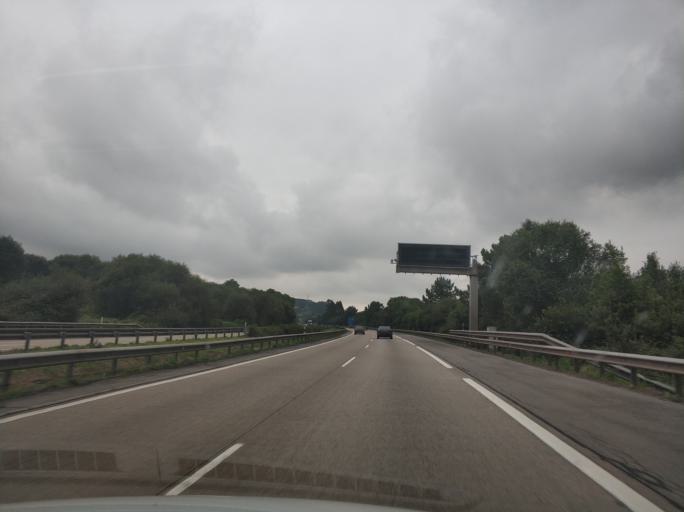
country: ES
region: Asturias
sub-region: Province of Asturias
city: Corvera de Asturias
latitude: 43.5259
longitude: -5.8253
